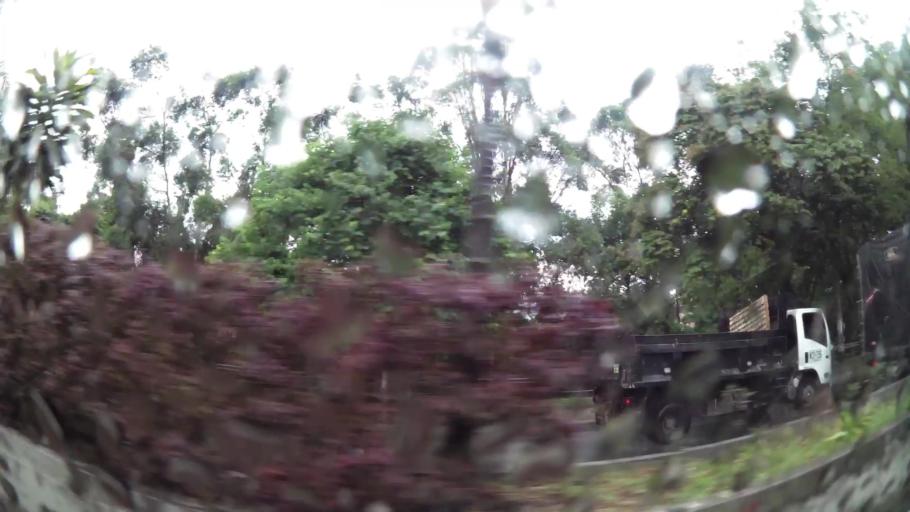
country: CO
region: Antioquia
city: Itagui
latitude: 6.1810
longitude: -75.6000
